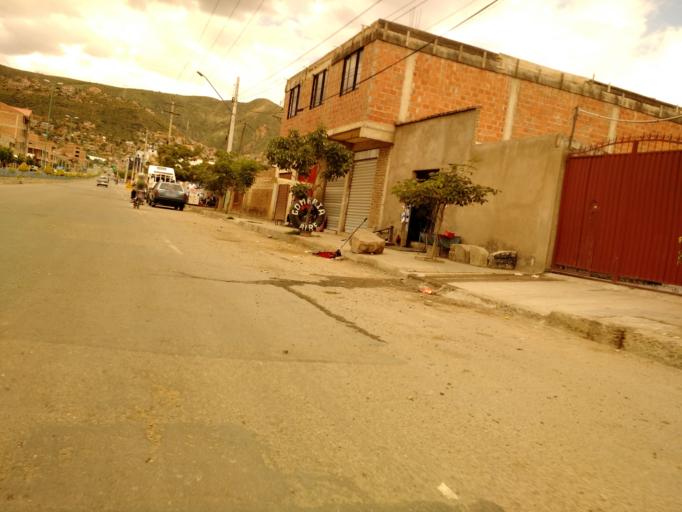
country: BO
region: Cochabamba
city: Cochabamba
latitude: -17.4233
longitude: -66.1275
